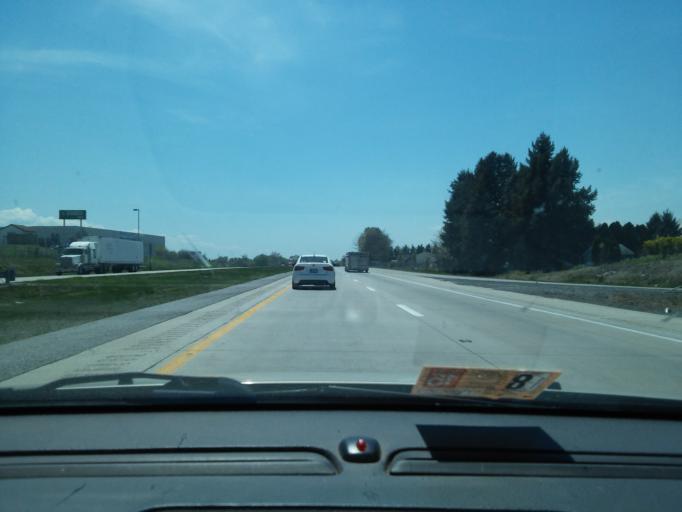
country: US
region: Pennsylvania
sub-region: Franklin County
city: Scotland
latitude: 39.9625
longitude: -77.5785
